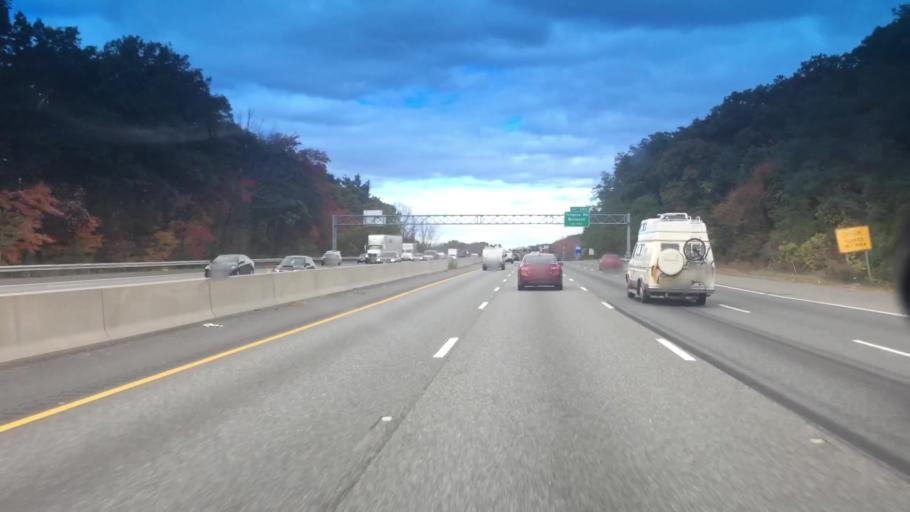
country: US
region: Massachusetts
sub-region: Middlesex County
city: Waltham
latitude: 42.4044
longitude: -71.2592
